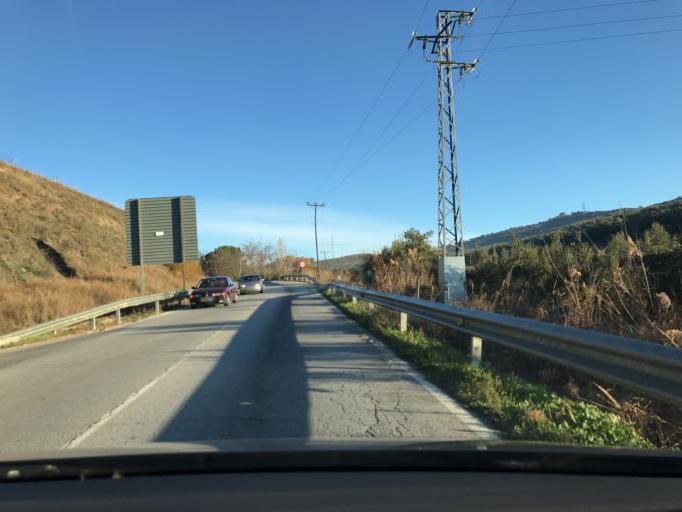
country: ES
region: Andalusia
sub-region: Provincia de Granada
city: Pulianas
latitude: 37.2398
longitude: -3.6061
